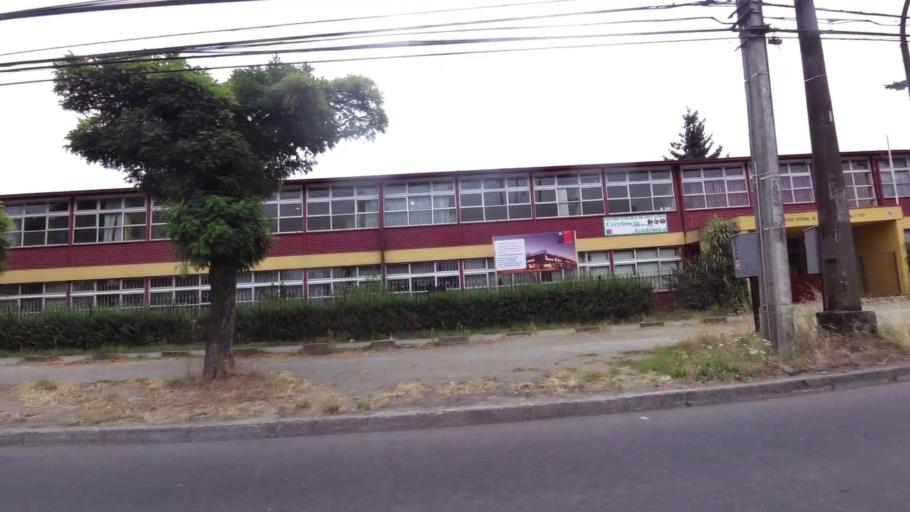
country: CL
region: Biobio
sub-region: Provincia de Concepcion
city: Concepcion
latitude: -36.8151
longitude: -73.0415
